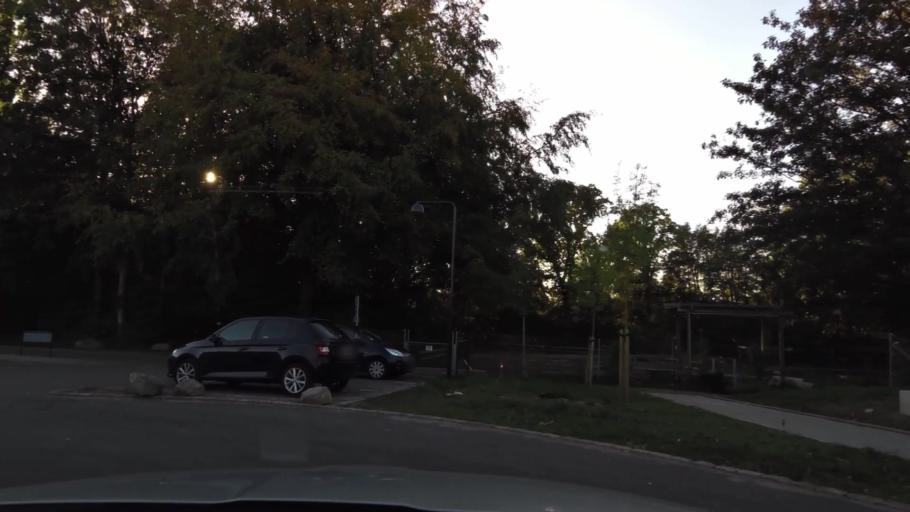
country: DK
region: Capital Region
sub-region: Lyngby-Tarbaek Kommune
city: Kongens Lyngby
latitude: 55.7532
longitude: 12.5080
